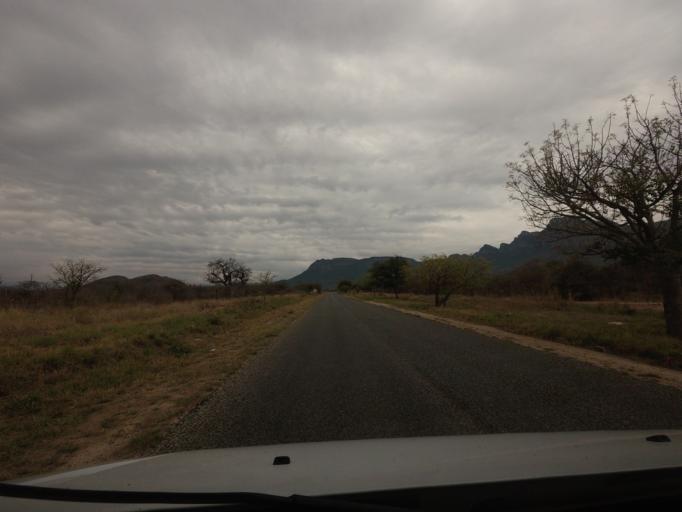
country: ZA
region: Limpopo
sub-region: Mopani District Municipality
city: Hoedspruit
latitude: -24.4918
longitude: 30.8909
